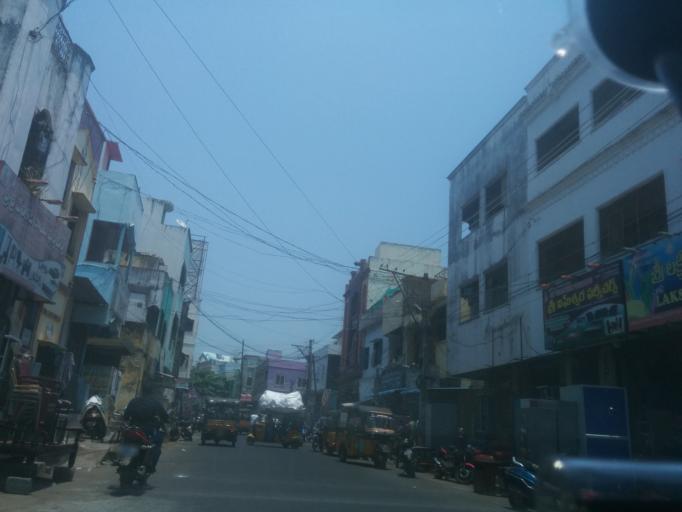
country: IN
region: Andhra Pradesh
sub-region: East Godavari
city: Rajahmundry
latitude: 16.9984
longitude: 81.7753
